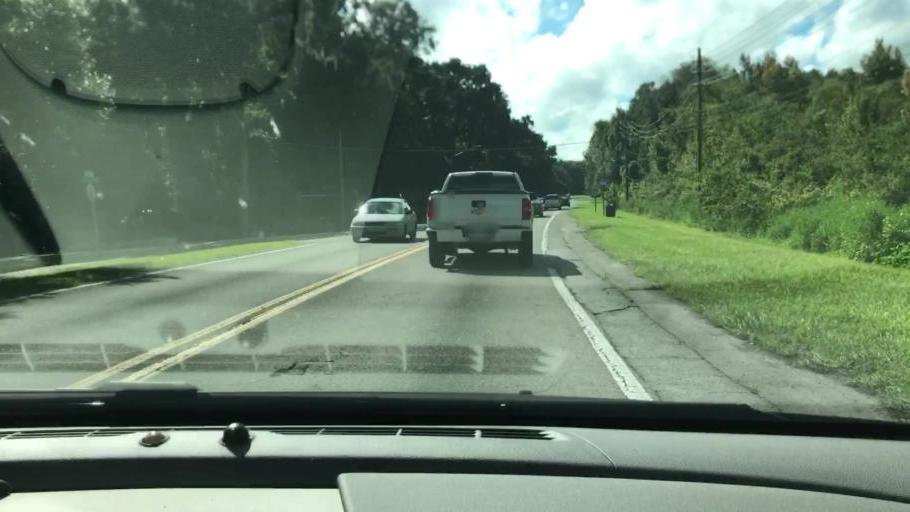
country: US
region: Florida
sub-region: Alachua County
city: Gainesville
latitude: 29.6482
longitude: -82.4022
